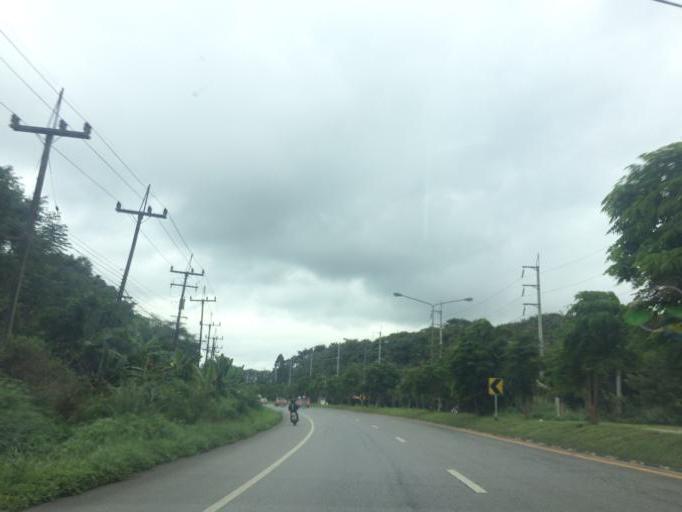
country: TH
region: Chiang Rai
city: Mae Chan
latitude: 20.1155
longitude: 99.8727
